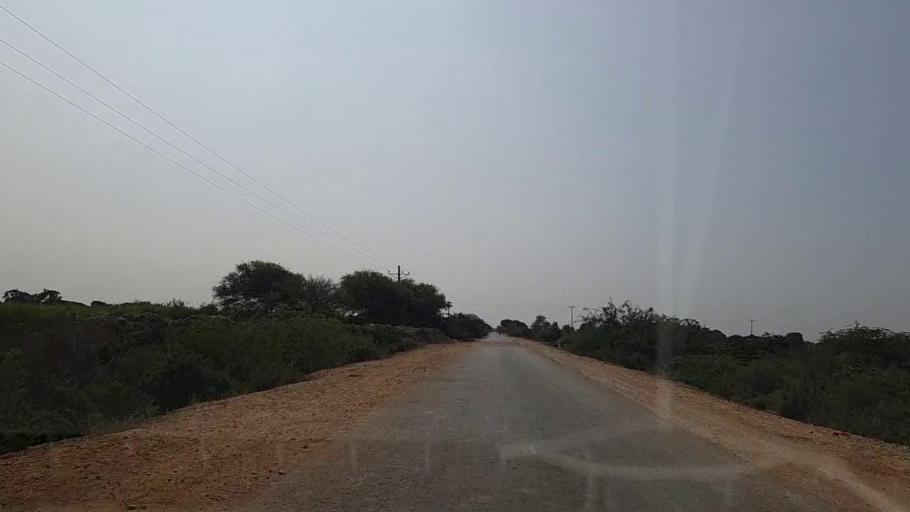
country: PK
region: Sindh
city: Chuhar Jamali
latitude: 24.2762
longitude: 67.9164
